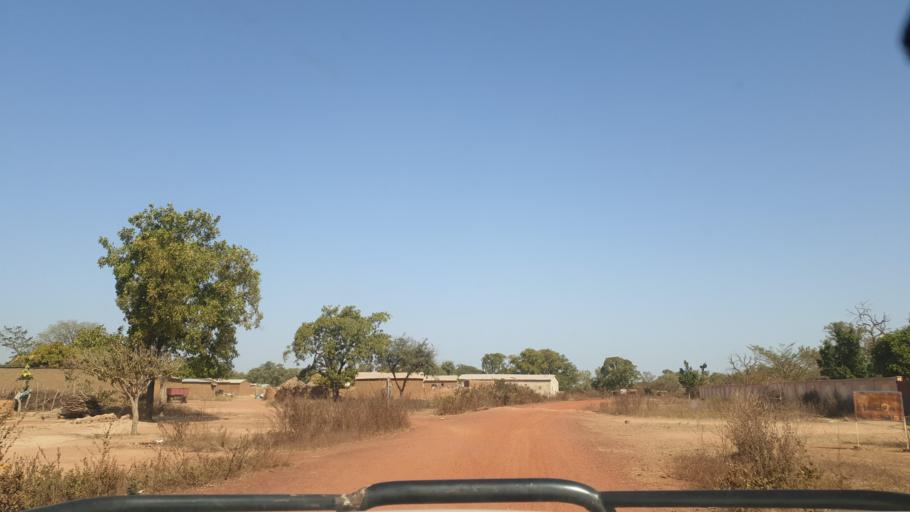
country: ML
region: Sikasso
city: Bougouni
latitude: 11.8279
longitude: -6.9793
